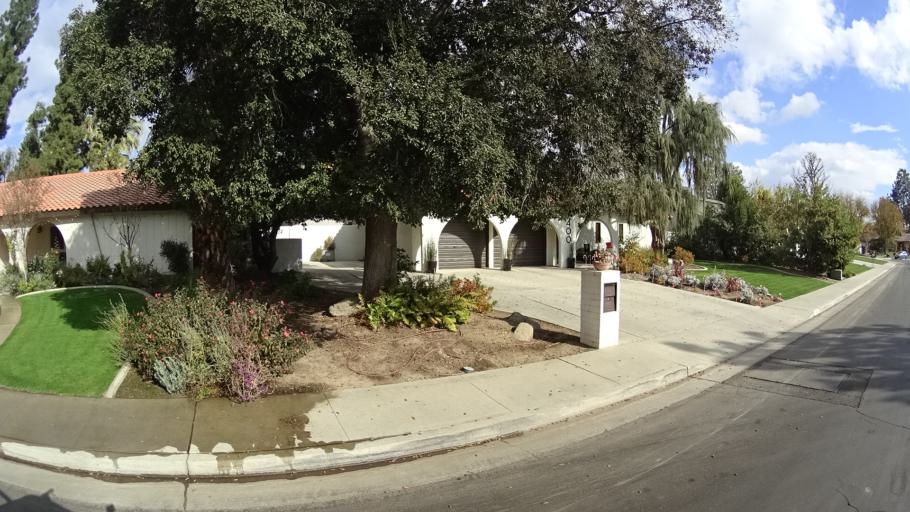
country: US
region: California
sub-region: Kern County
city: Greenacres
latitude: 35.3474
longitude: -119.0851
